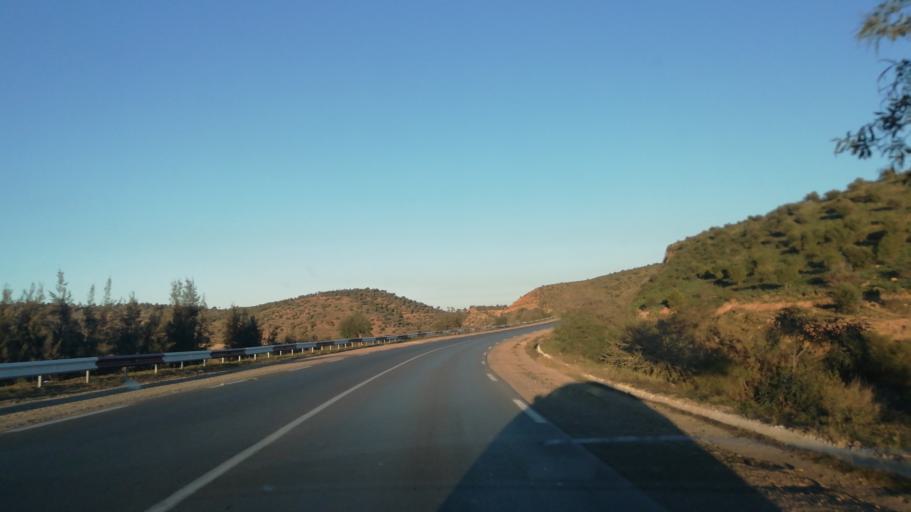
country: DZ
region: Tlemcen
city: Nedroma
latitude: 34.8655
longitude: -1.6772
